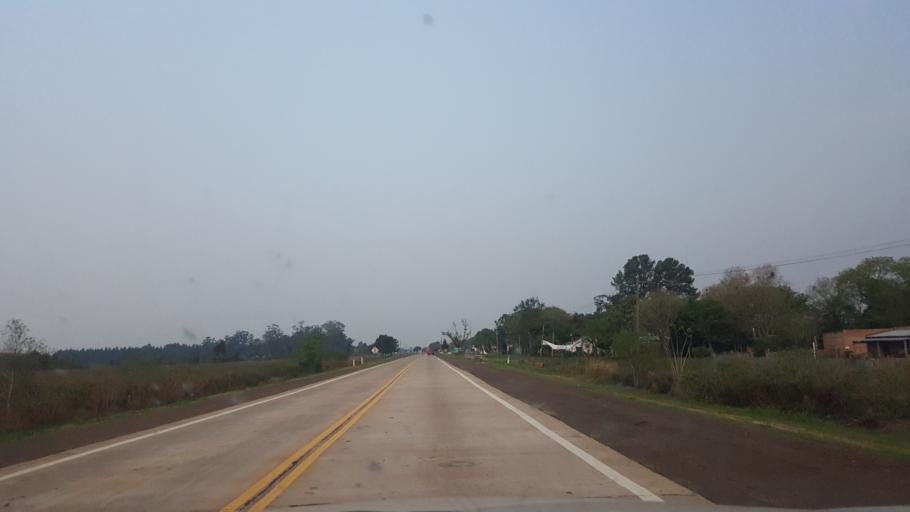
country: PY
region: Misiones
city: Ayolas
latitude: -27.6292
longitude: -56.9098
